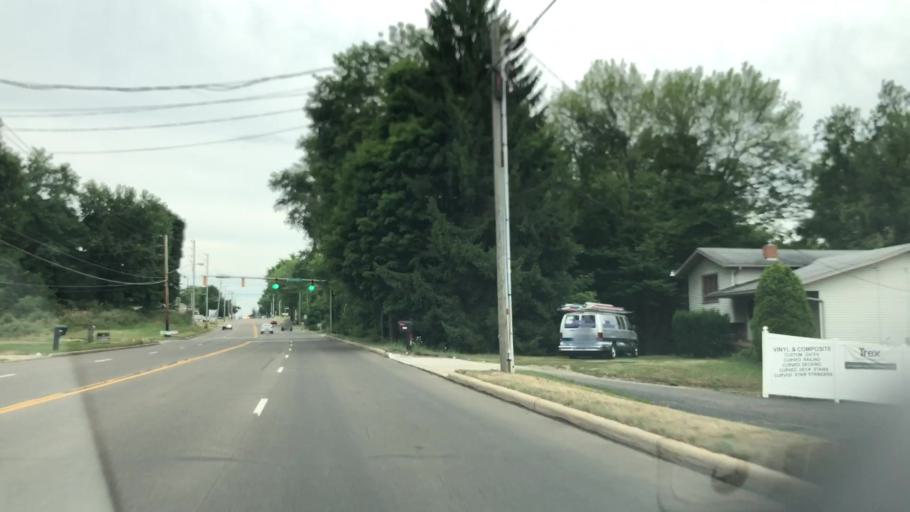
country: US
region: Ohio
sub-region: Stark County
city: Greentown
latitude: 40.9157
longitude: -81.4052
